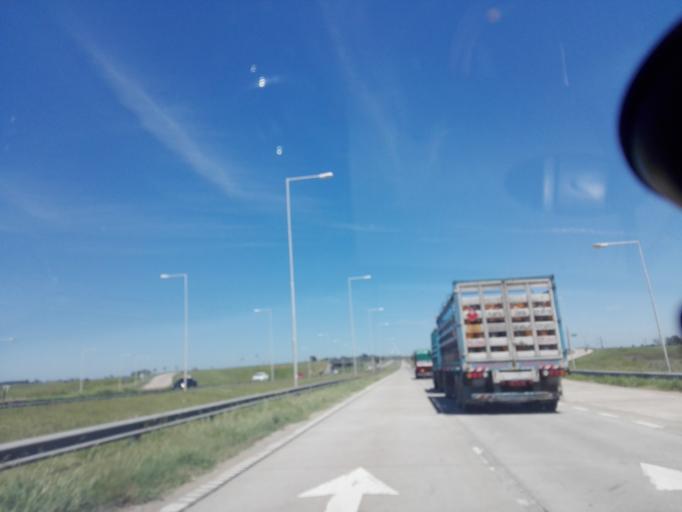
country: AR
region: Santa Fe
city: Canada de Gomez
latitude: -32.8470
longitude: -61.3878
